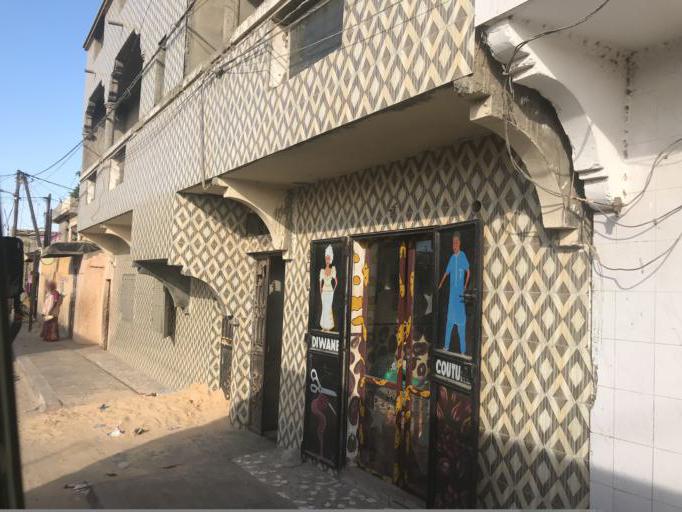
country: SN
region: Saint-Louis
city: Saint-Louis
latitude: 16.0004
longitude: -16.4965
